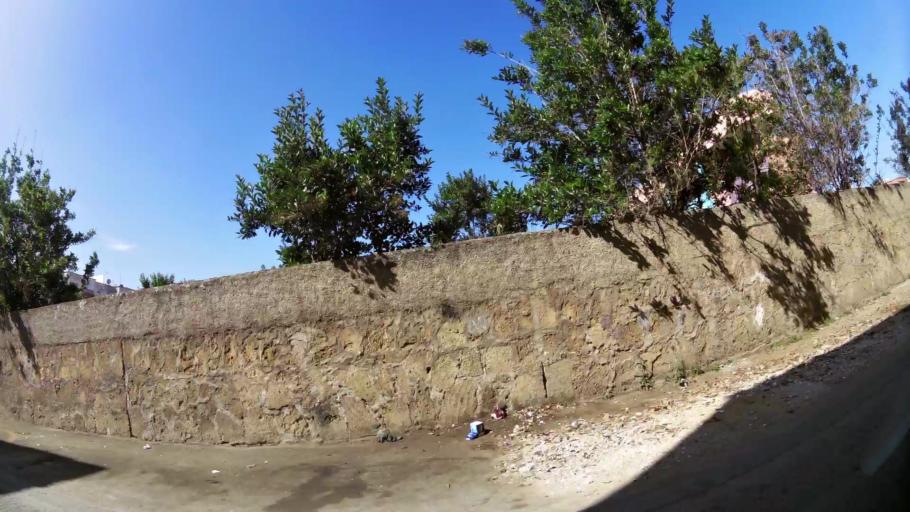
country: MA
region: Rabat-Sale-Zemmour-Zaer
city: Sale
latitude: 34.0647
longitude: -6.7989
